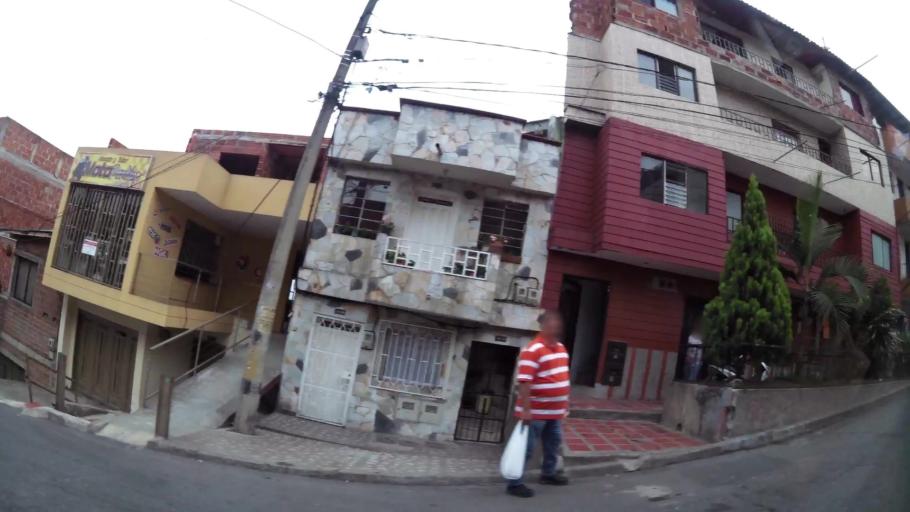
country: CO
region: Antioquia
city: Medellin
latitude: 6.2341
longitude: -75.5552
